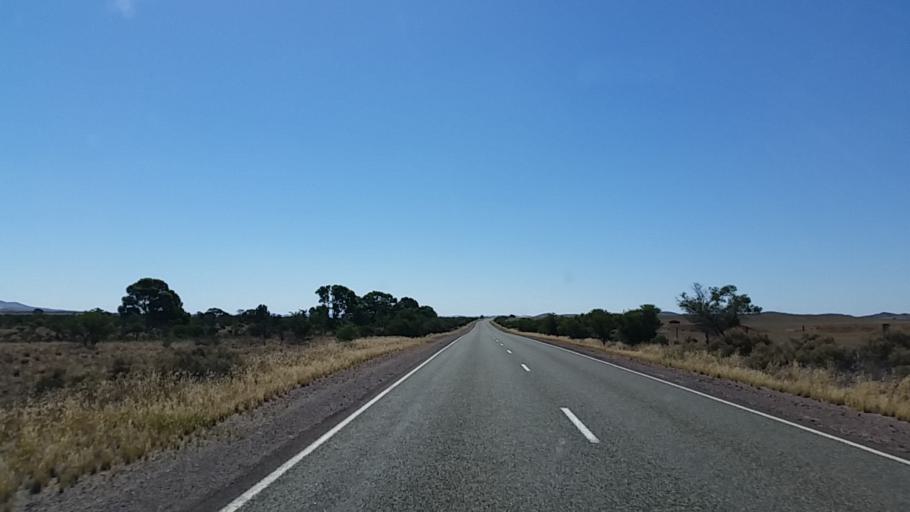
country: AU
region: South Australia
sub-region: Flinders Ranges
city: Quorn
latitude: -32.4572
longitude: 138.5376
